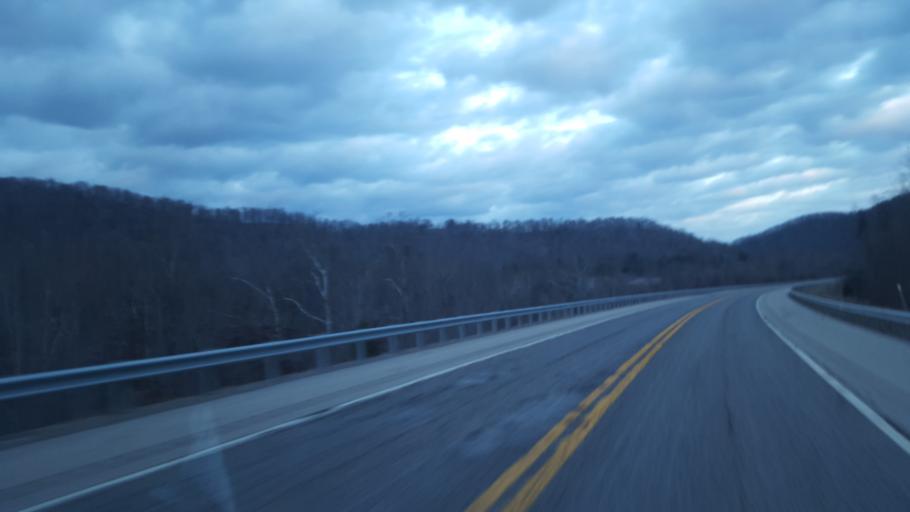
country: US
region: Kentucky
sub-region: Lewis County
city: Vanceburg
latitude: 38.5970
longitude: -83.3387
